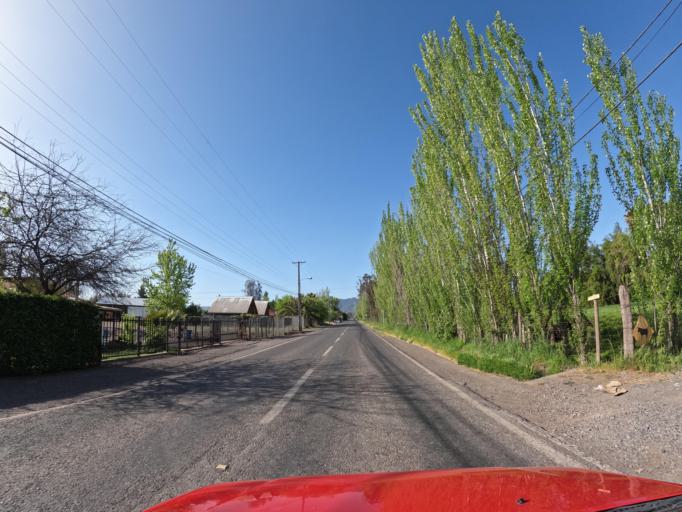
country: CL
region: Maule
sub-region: Provincia de Curico
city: Rauco
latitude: -34.8842
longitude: -71.2713
